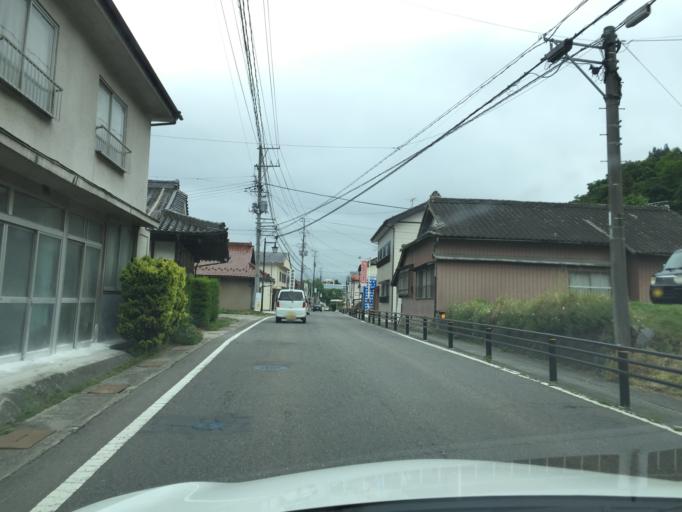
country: JP
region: Fukushima
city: Funehikimachi-funehiki
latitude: 37.3851
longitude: 140.6299
